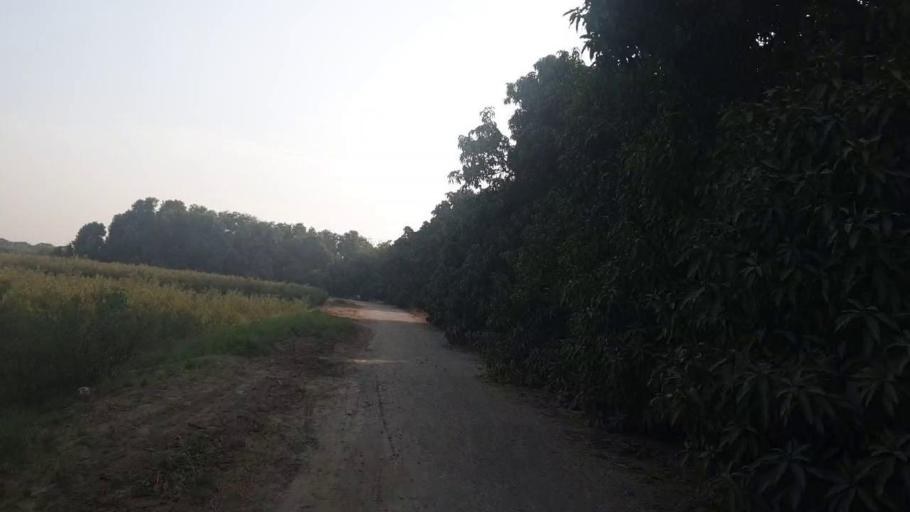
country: PK
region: Sindh
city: Tando Jam
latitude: 25.4232
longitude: 68.4690
